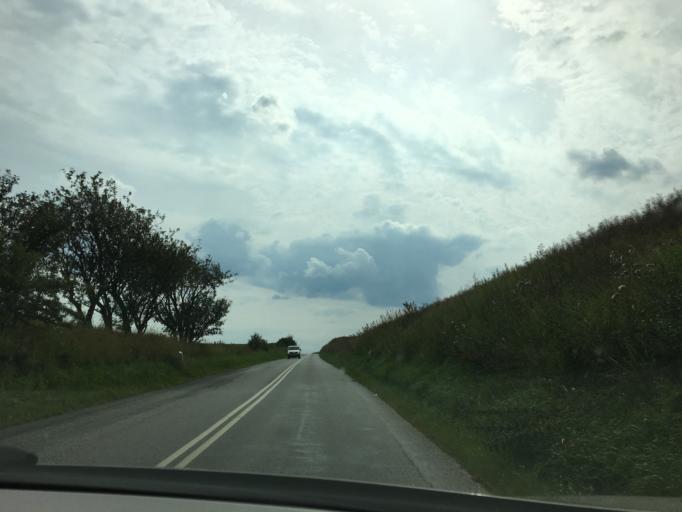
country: DK
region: Central Jutland
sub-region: Viborg Kommune
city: Stoholm
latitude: 56.4700
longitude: 9.1462
